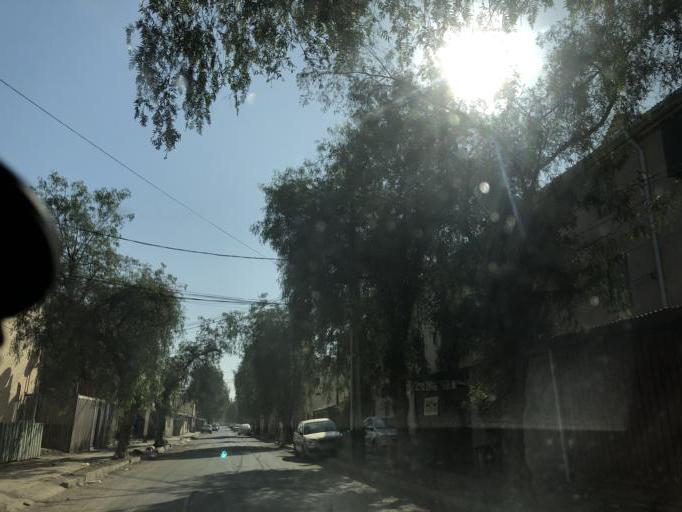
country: CL
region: Santiago Metropolitan
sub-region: Provincia de Santiago
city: La Pintana
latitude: -33.6284
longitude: -70.6211
